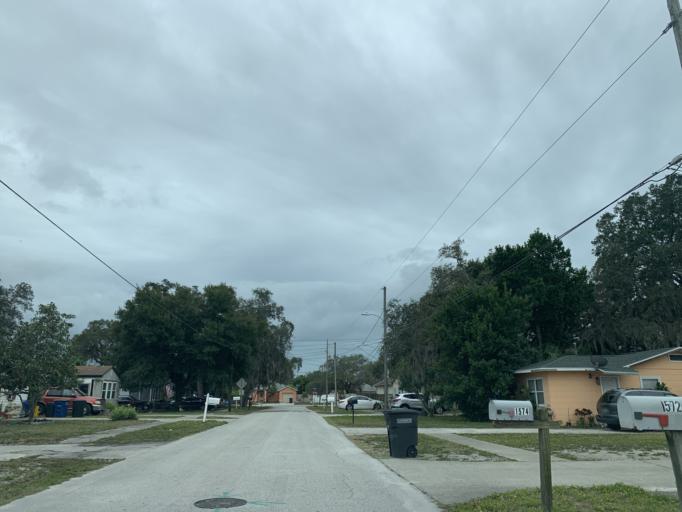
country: US
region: Florida
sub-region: Pinellas County
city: Belleair
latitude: 27.9399
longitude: -82.7891
